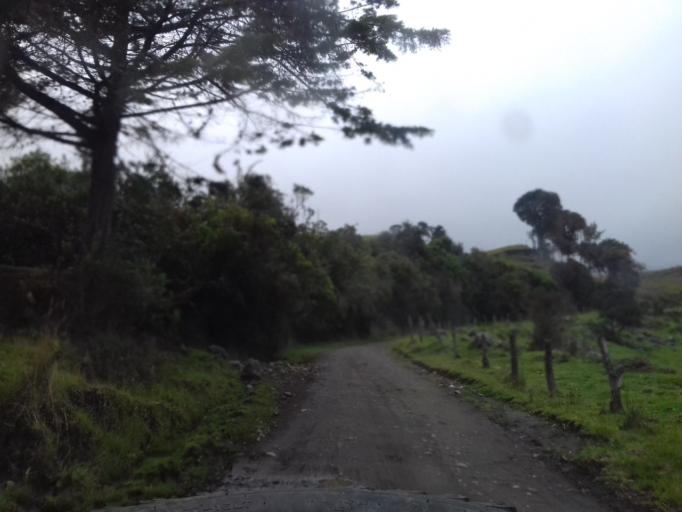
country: CO
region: Tolima
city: Murillo
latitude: 4.8959
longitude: -75.2376
